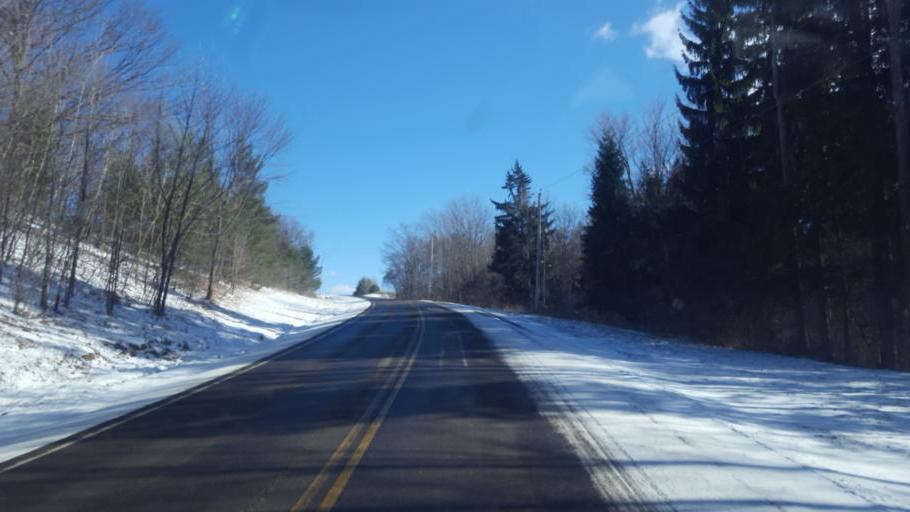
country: US
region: New York
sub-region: Allegany County
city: Friendship
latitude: 42.1875
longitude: -78.0896
